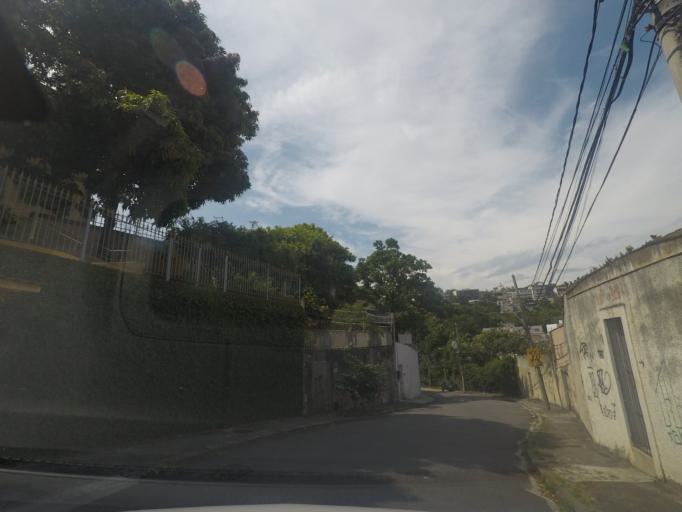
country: BR
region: Rio de Janeiro
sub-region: Rio De Janeiro
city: Rio de Janeiro
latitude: -22.8175
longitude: -43.1979
